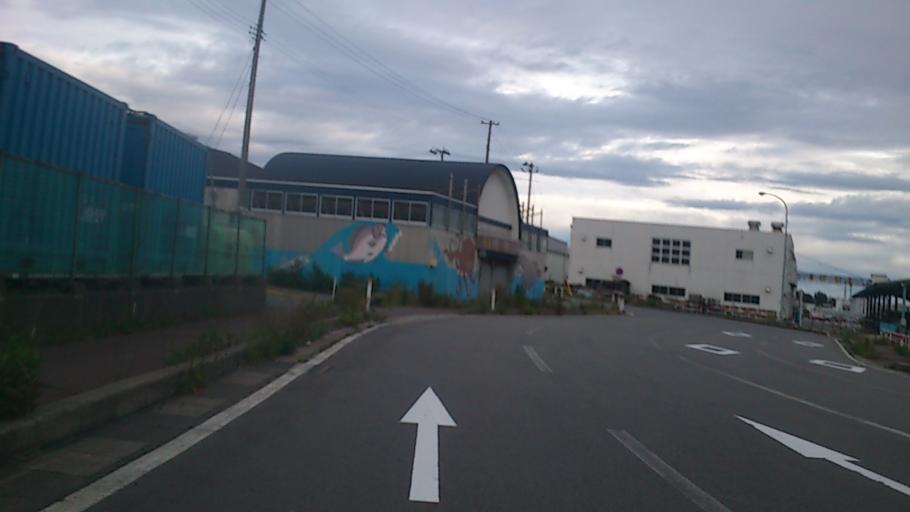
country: JP
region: Akita
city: Akita Shi
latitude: 39.7515
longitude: 140.0627
